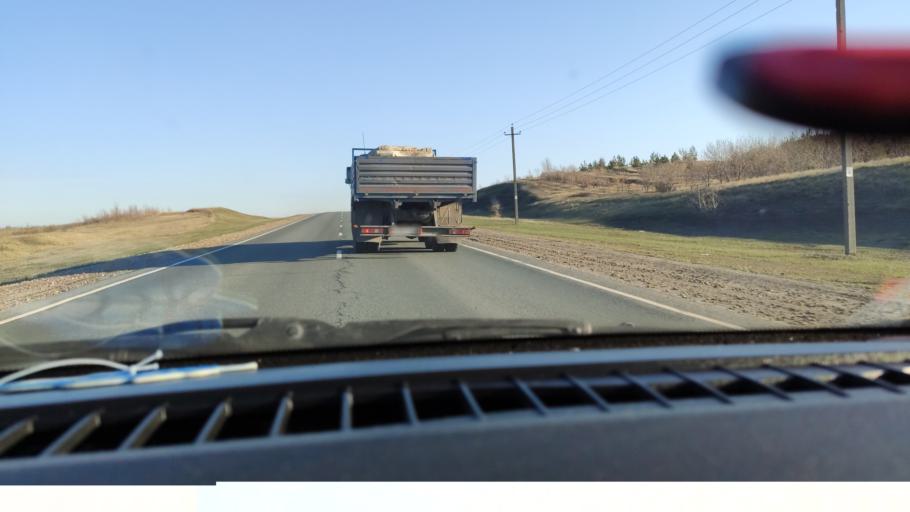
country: RU
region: Saratov
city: Alekseyevka
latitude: 52.3006
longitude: 47.9269
